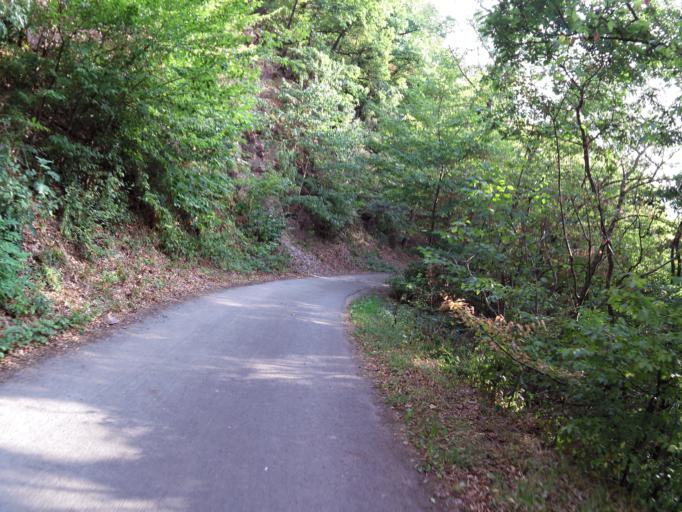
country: DE
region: North Rhine-Westphalia
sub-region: Regierungsbezirk Koln
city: Nideggen
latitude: 50.6815
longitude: 6.4721
